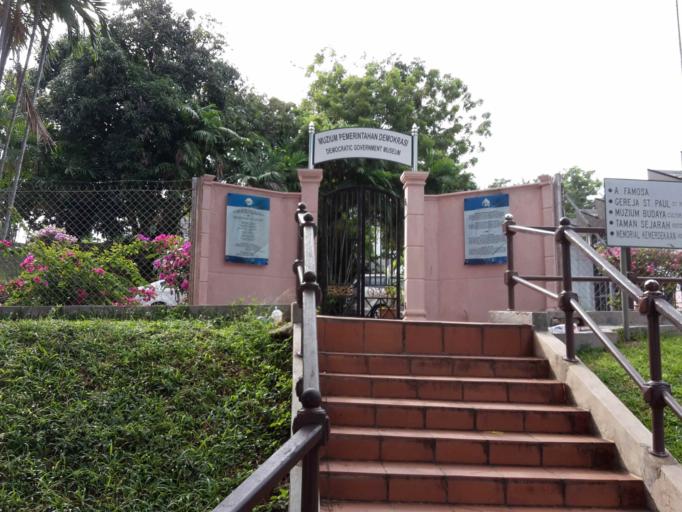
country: MY
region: Melaka
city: Malacca
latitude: 2.1936
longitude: 102.2490
